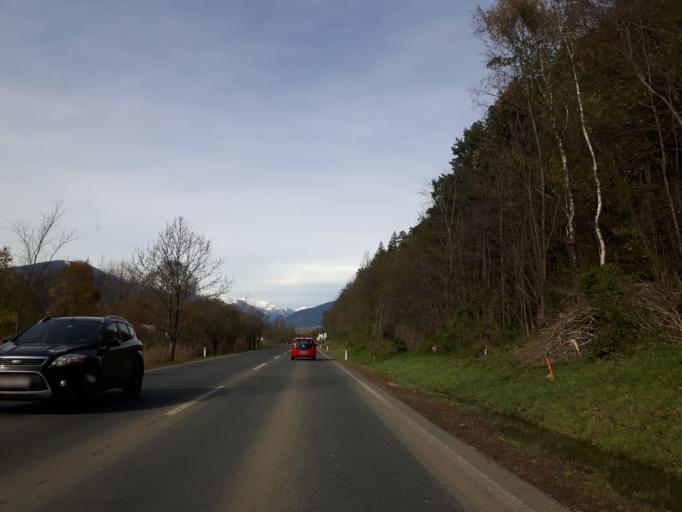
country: AT
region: Tyrol
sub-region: Politischer Bezirk Lienz
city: Lavant
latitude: 46.8057
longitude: 12.8625
